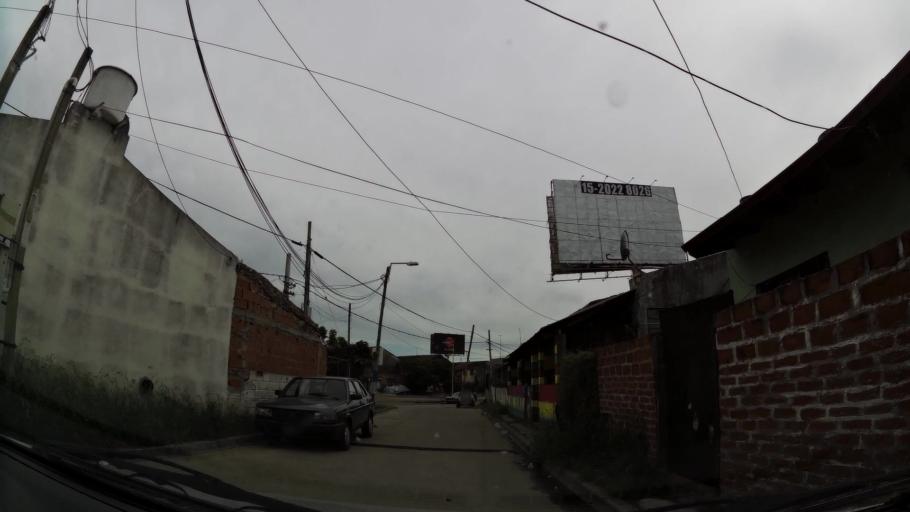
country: AR
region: Buenos Aires
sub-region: Partido de Avellaneda
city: Avellaneda
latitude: -34.6446
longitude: -58.3510
